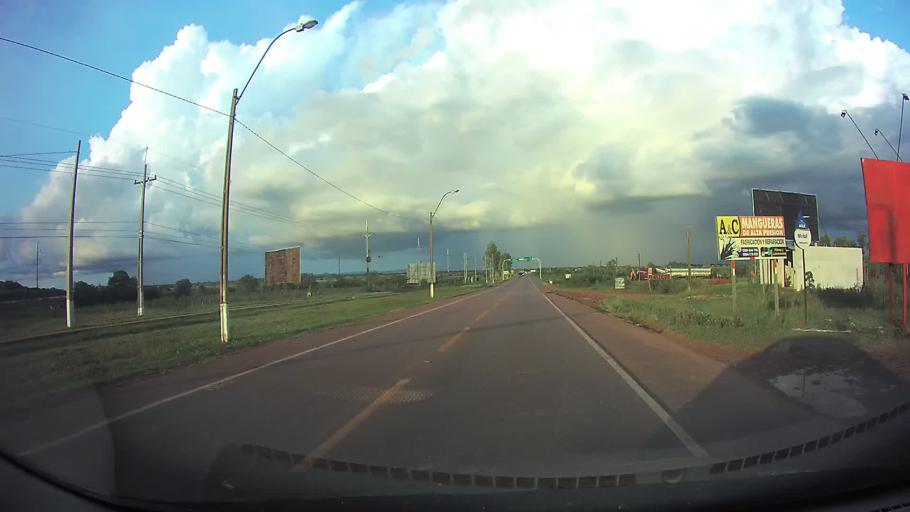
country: PY
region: Paraguari
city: Carapegua
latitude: -25.7610
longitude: -57.2322
